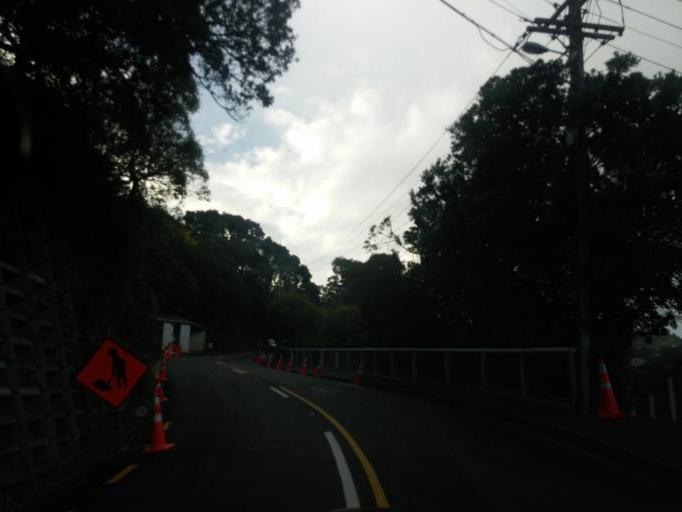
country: NZ
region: Wellington
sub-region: Wellington City
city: Kelburn
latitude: -41.2652
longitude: 174.7779
